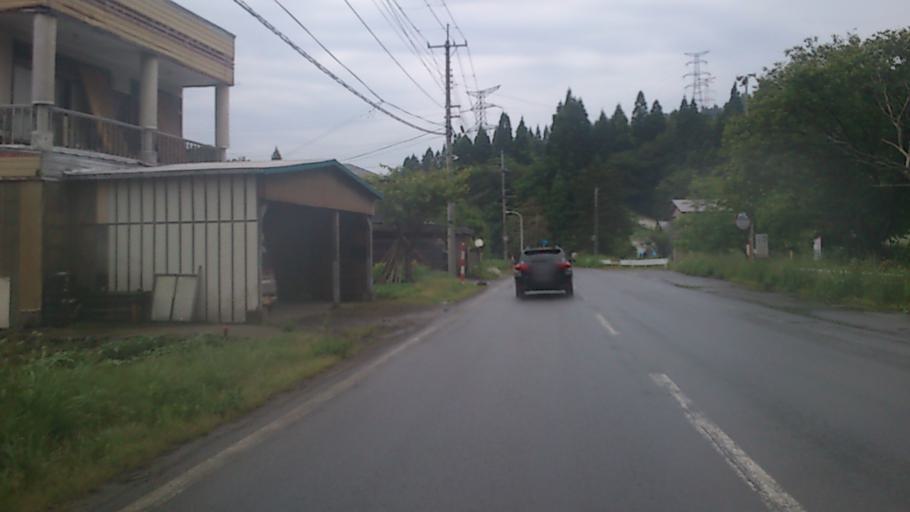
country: JP
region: Akita
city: Takanosu
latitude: 40.2437
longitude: 140.2468
